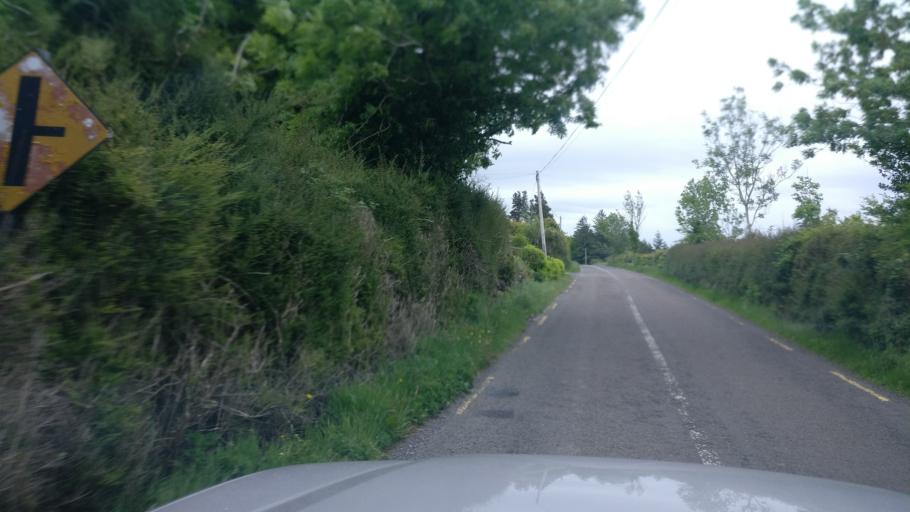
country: IE
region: Connaught
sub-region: County Galway
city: Loughrea
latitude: 53.0865
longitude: -8.4984
